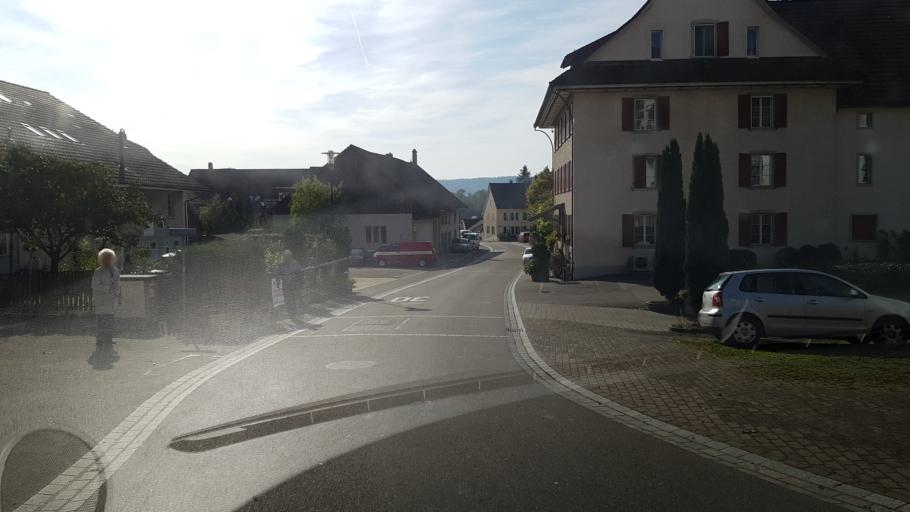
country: CH
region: Aargau
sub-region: Bezirk Baden
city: Birmenstorf
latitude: 47.4614
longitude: 8.2481
